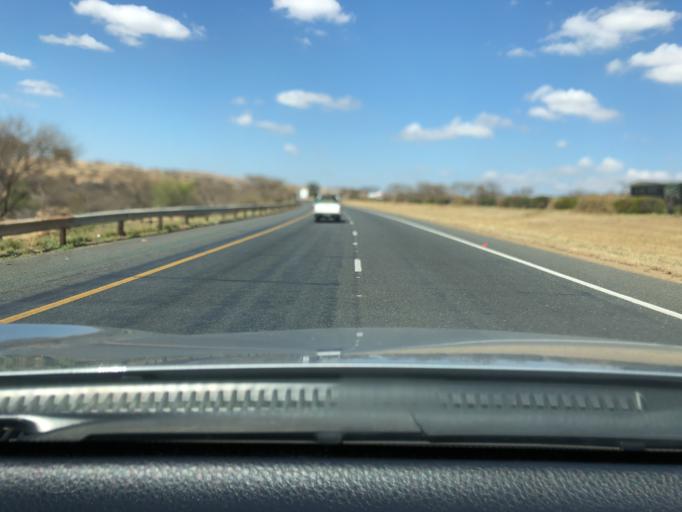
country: ZA
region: KwaZulu-Natal
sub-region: uThukela District Municipality
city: Estcourt
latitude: -28.9712
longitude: 29.7936
